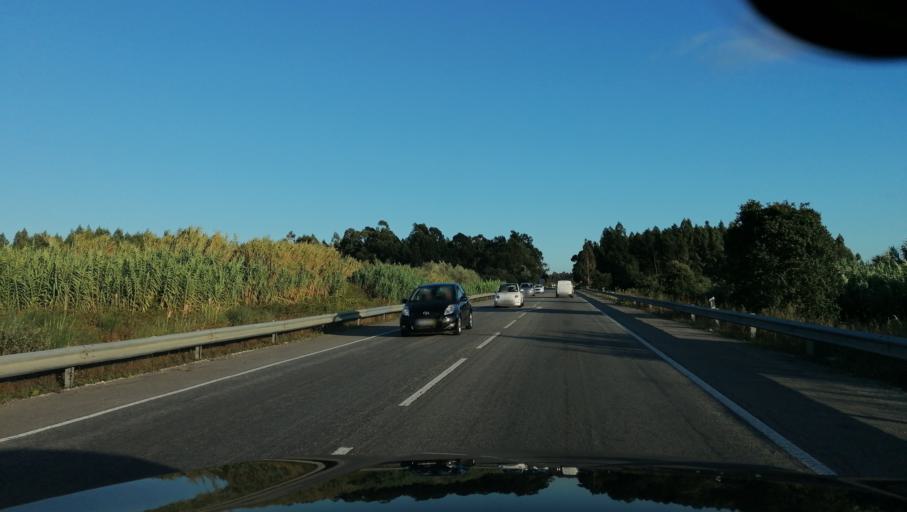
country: PT
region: Aveiro
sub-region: Aveiro
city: Aradas
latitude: 40.6081
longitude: -8.6237
